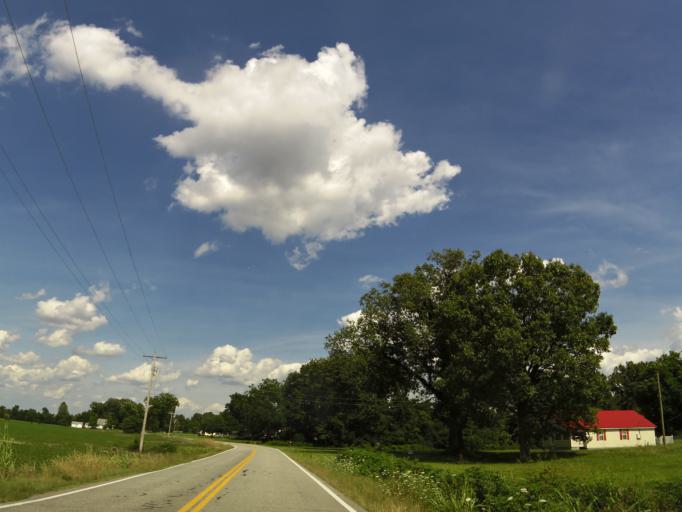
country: US
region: Tennessee
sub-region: Gibson County
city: Milan
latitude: 35.9764
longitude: -88.8131
